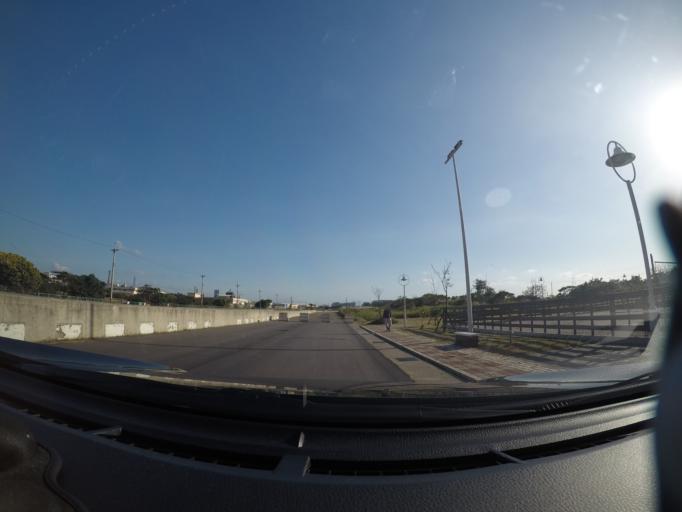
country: TW
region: Taiwan
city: Taoyuan City
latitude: 25.1073
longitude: 121.2539
